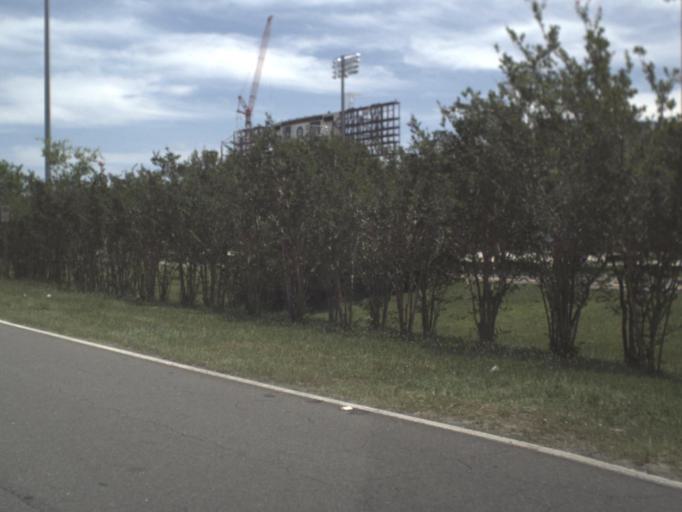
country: US
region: Florida
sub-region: Duval County
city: Jacksonville
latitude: 30.3276
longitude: -81.6396
